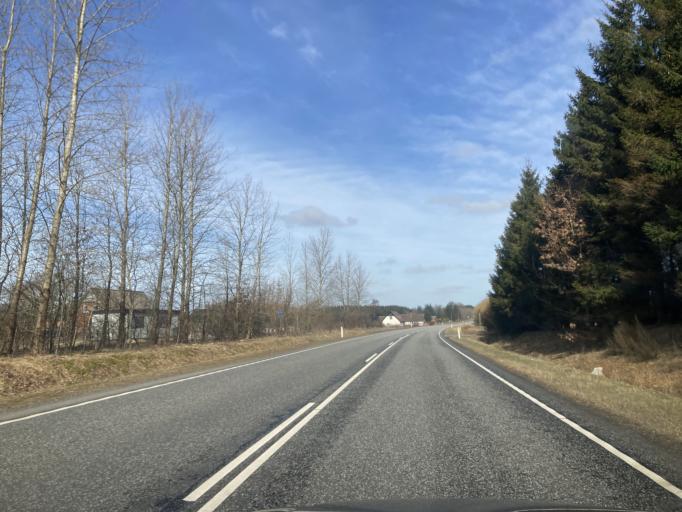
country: DK
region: Central Jutland
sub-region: Hedensted Kommune
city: Torring
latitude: 55.9775
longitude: 9.3945
